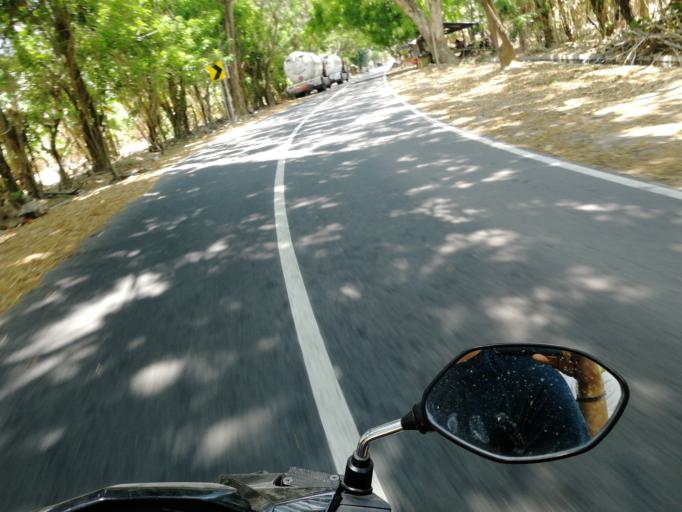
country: ID
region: West Nusa Tenggara
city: Karangsubagan
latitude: -8.4434
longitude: 116.0413
